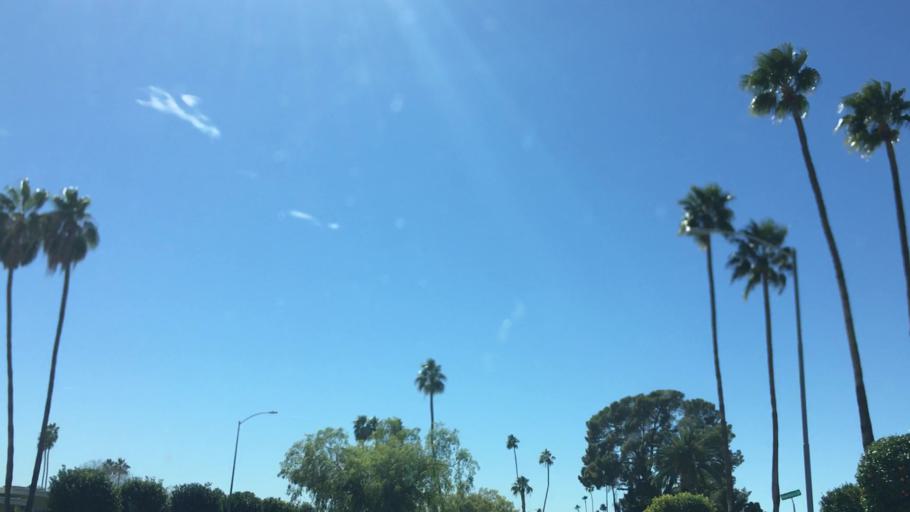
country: US
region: Arizona
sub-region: Maricopa County
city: Sun City
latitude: 33.6067
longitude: -112.2743
